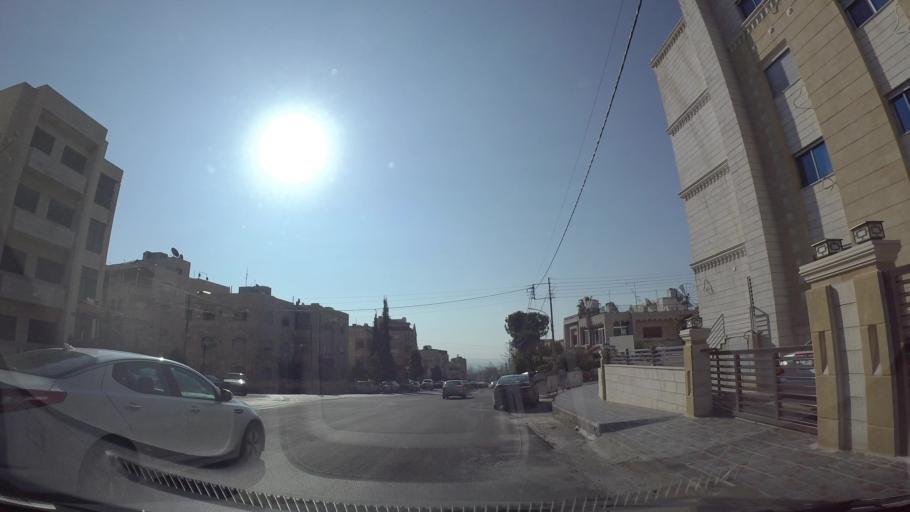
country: JO
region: Amman
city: Al Jubayhah
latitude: 32.0001
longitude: 35.8857
